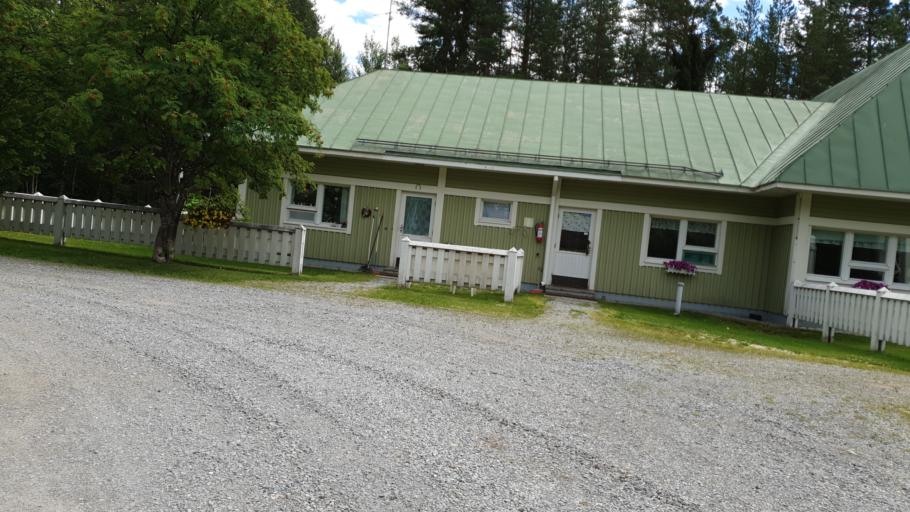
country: FI
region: Kainuu
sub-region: Kehys-Kainuu
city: Kuhmo
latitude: 64.3895
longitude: 29.8266
